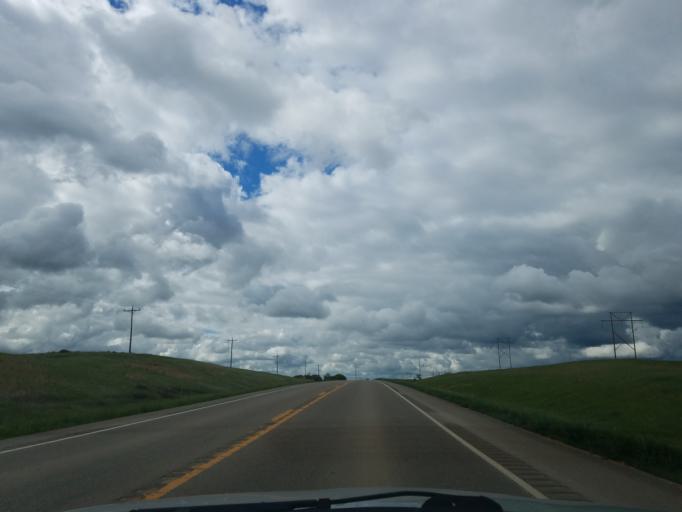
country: US
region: North Dakota
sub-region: McKenzie County
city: Watford City
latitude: 47.6913
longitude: -103.2833
